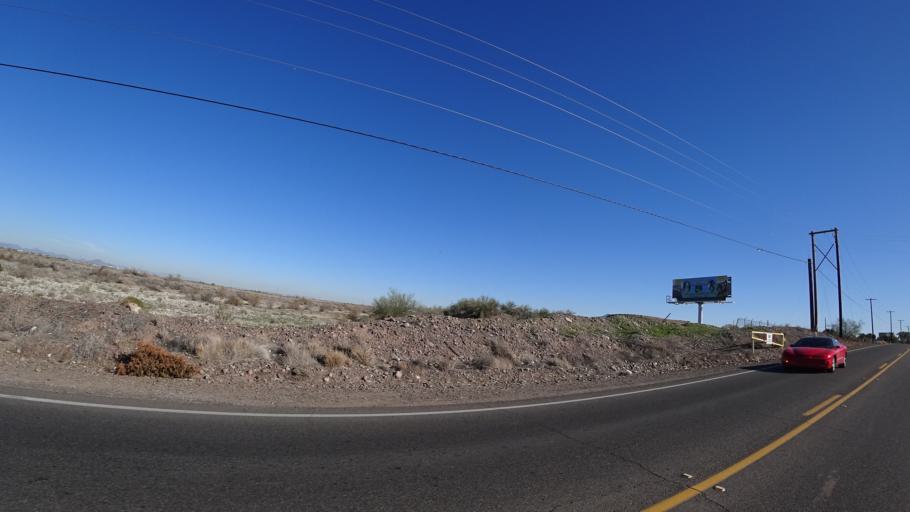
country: US
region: Arizona
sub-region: Maricopa County
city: Laveen
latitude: 33.3954
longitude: -112.2033
